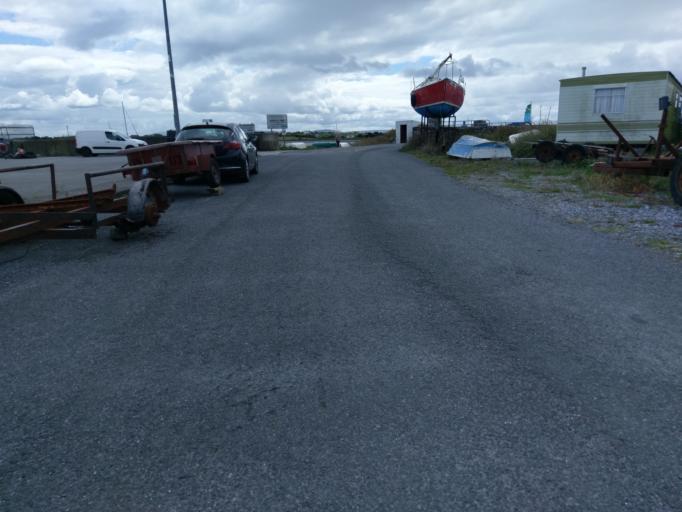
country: IE
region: Connaught
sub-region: County Galway
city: Oranmore
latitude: 53.2444
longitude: -8.9676
